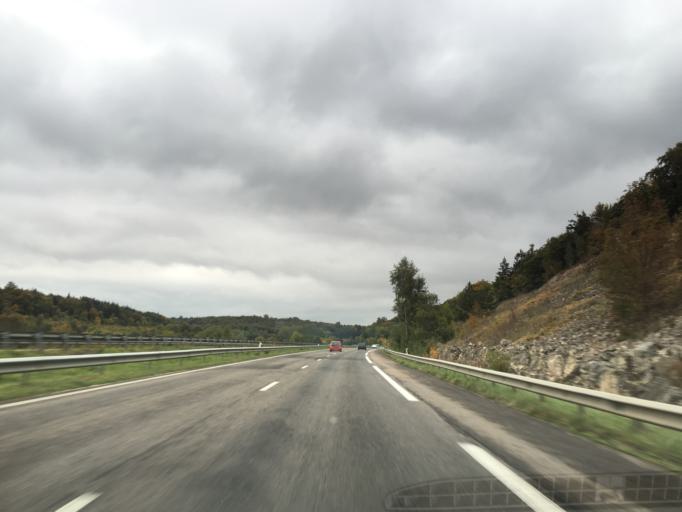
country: FR
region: Lorraine
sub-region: Departement de la Meuse
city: Vacon
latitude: 48.6871
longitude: 5.5725
